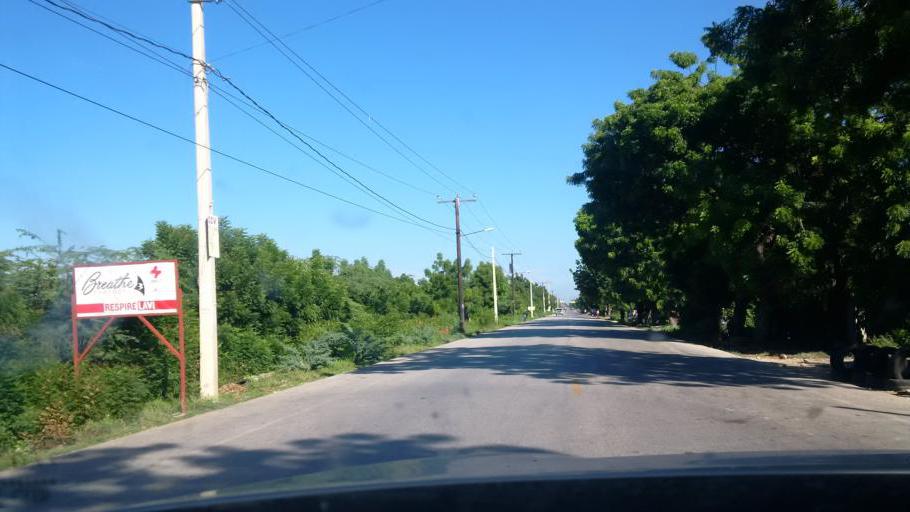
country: HT
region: Ouest
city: Cabaret
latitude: 18.7646
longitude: -72.4625
